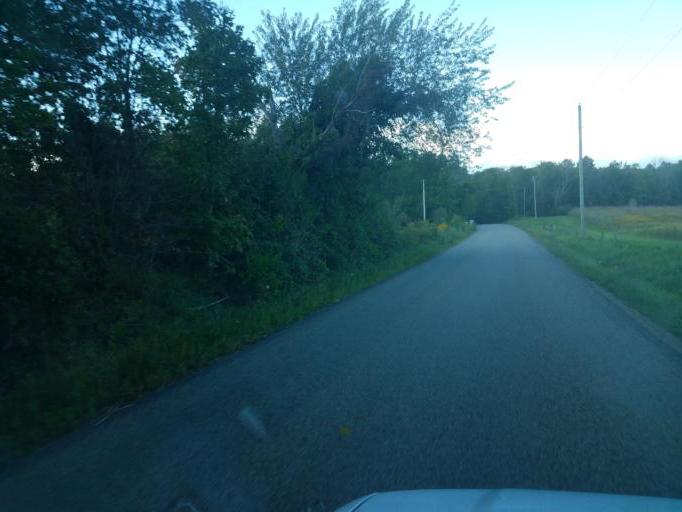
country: US
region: Ohio
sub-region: Knox County
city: Fredericktown
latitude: 40.3952
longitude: -82.5998
